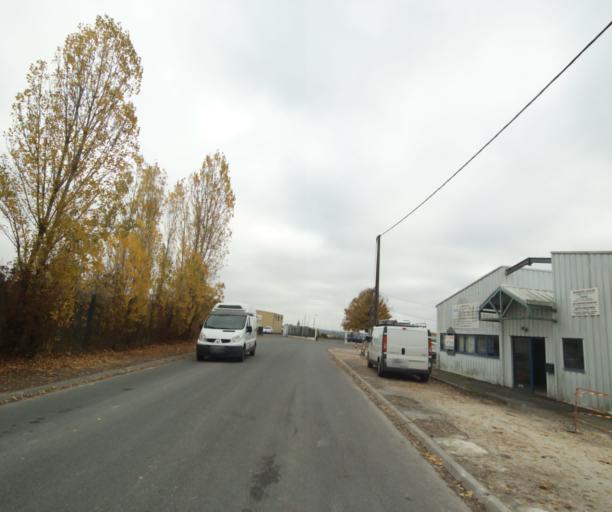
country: FR
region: Poitou-Charentes
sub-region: Departement de la Charente-Maritime
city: Saintes
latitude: 45.7432
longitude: -0.6633
